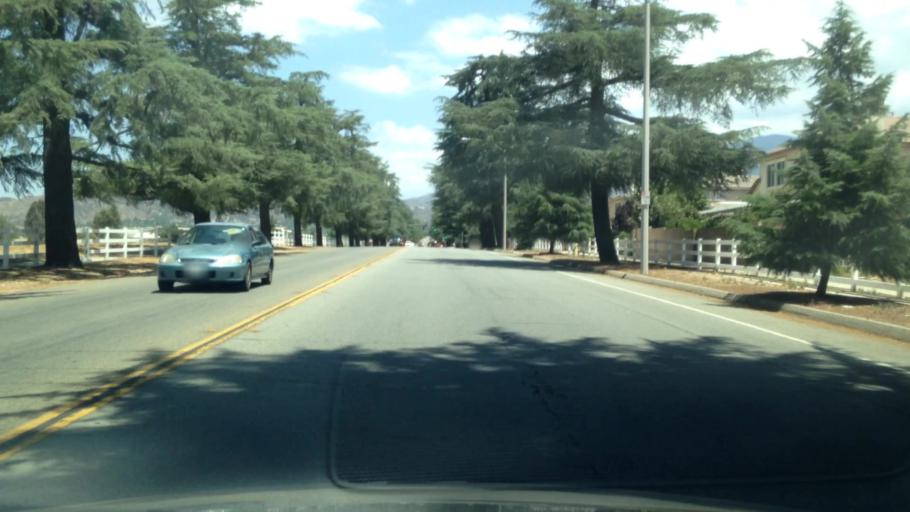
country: US
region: California
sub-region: Riverside County
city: Cherry Valley
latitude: 33.9514
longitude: -116.9772
